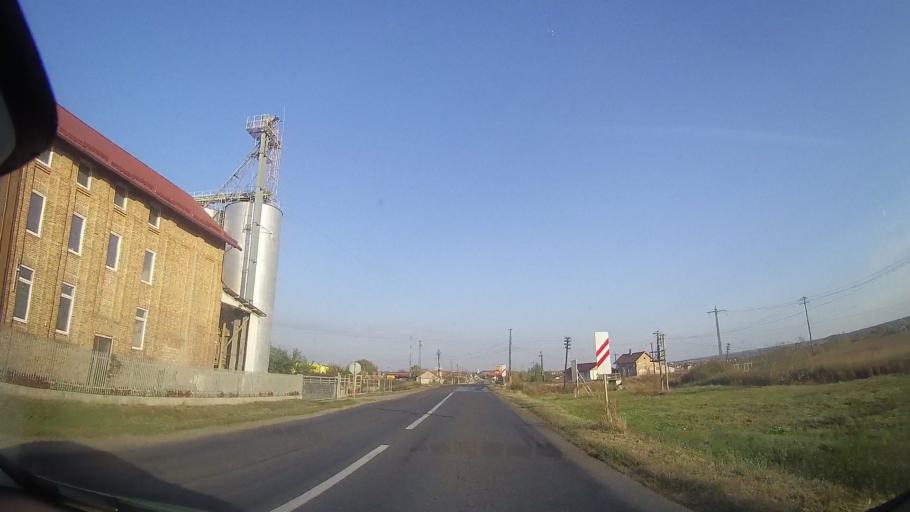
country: RO
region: Timis
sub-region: Comuna Pischia
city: Pischia
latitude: 45.8955
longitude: 21.3444
